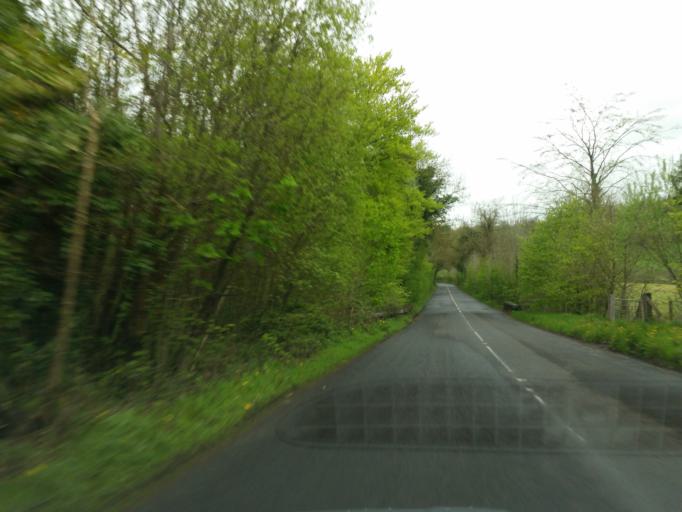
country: GB
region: Northern Ireland
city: Lisnaskea
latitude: 54.2244
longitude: -7.3511
